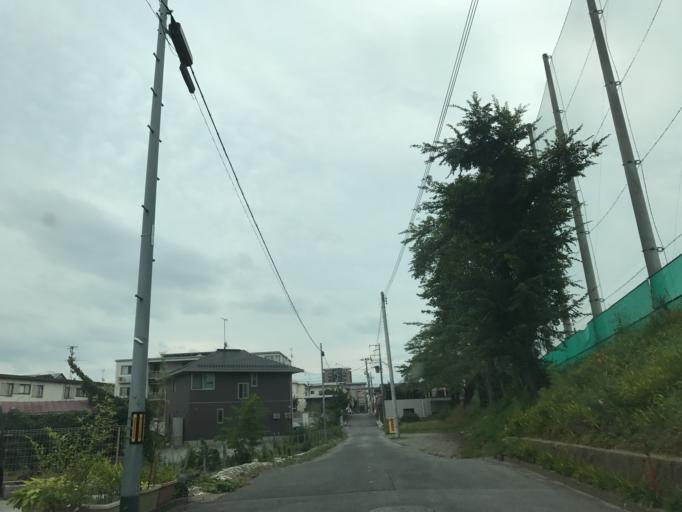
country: JP
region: Fukushima
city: Koriyama
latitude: 37.4048
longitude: 140.3733
